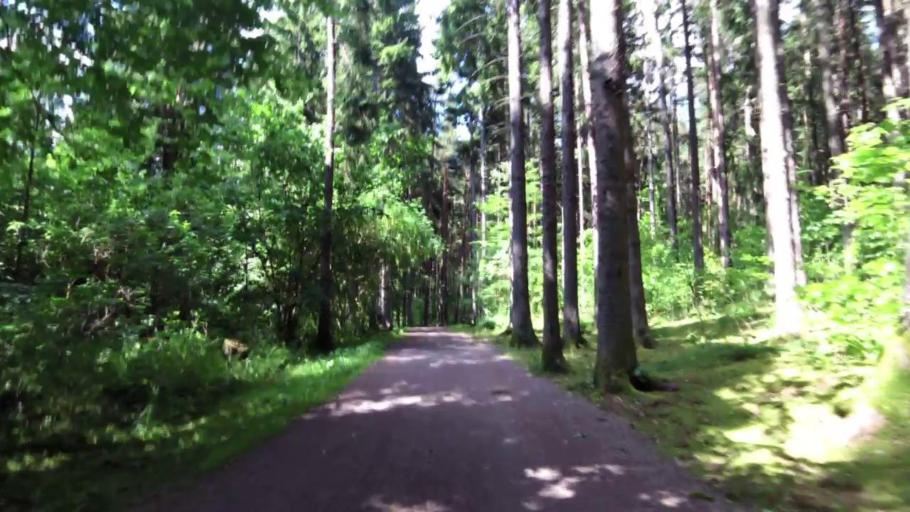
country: SE
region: OEstergoetland
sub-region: Linkopings Kommun
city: Linkoping
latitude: 58.4157
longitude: 15.5831
